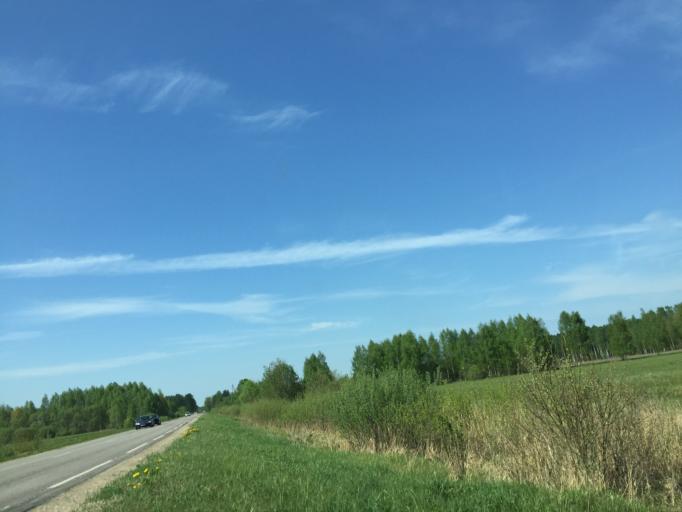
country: LV
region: Jelgava
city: Jelgava
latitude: 56.7298
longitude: 23.6823
